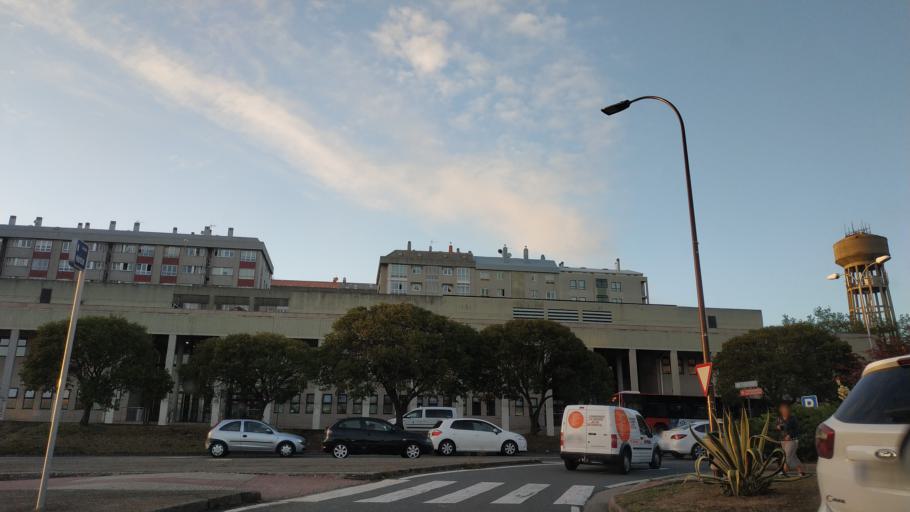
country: ES
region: Galicia
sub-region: Provincia da Coruna
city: A Coruna
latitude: 43.3576
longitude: -8.4226
